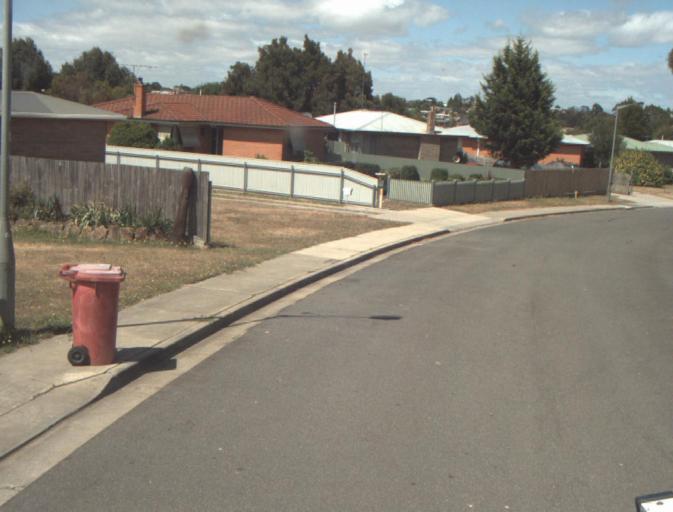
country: AU
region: Tasmania
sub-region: Launceston
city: Newstead
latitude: -41.4144
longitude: 147.1766
